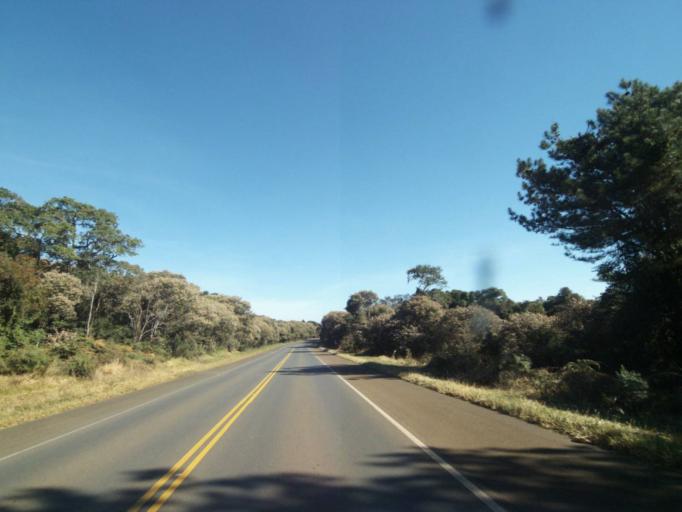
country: BR
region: Parana
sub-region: Tibagi
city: Tibagi
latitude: -24.4247
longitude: -50.3964
